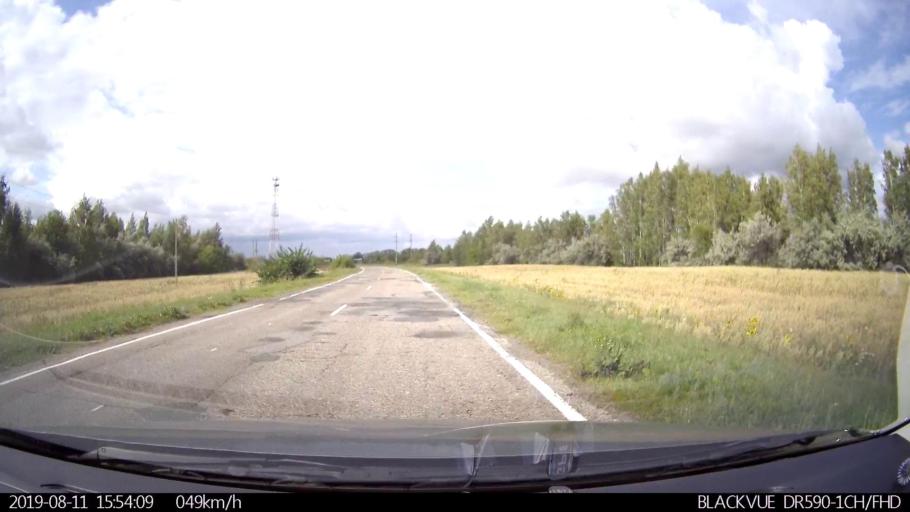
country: RU
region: Ulyanovsk
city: Ignatovka
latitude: 53.9393
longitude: 47.6568
